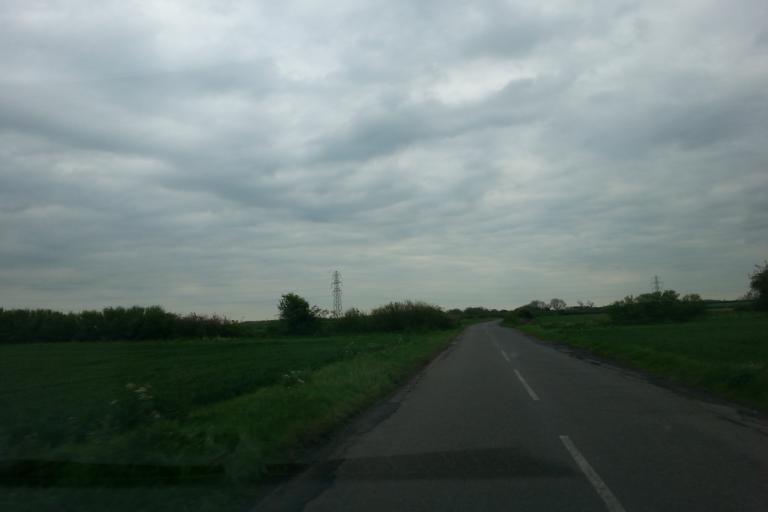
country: GB
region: England
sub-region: Nottinghamshire
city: Farndon
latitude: 53.0059
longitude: -0.8368
